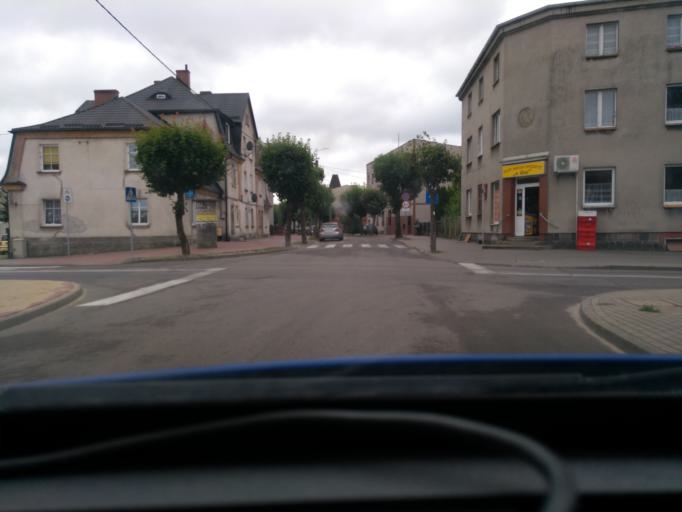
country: PL
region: Pomeranian Voivodeship
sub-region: Powiat kartuski
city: Kartuzy
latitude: 54.3385
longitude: 18.2005
